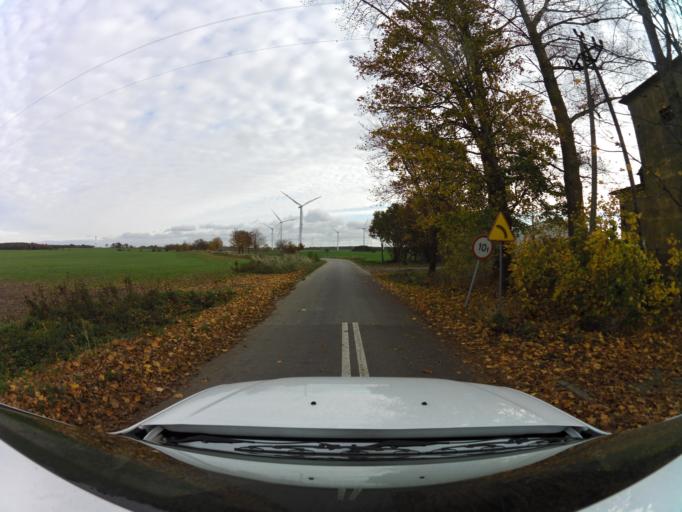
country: PL
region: West Pomeranian Voivodeship
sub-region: Powiat gryficki
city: Karnice
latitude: 54.0493
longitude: 15.0746
